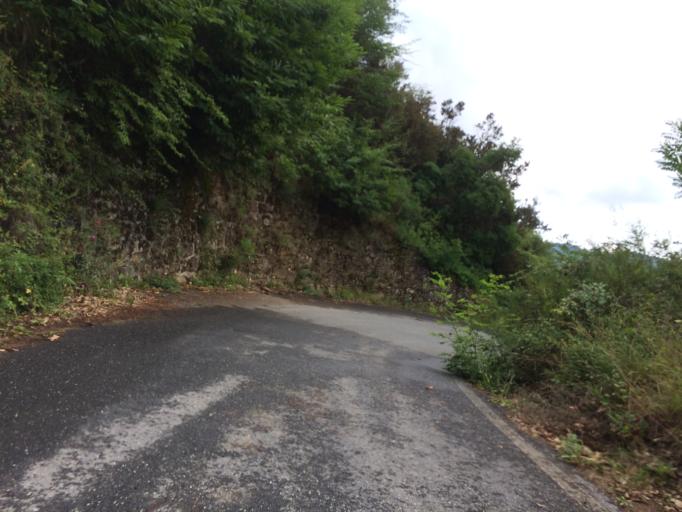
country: IT
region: Liguria
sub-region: Provincia di Imperia
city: Castel Vittorio
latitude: 43.9464
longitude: 7.6887
